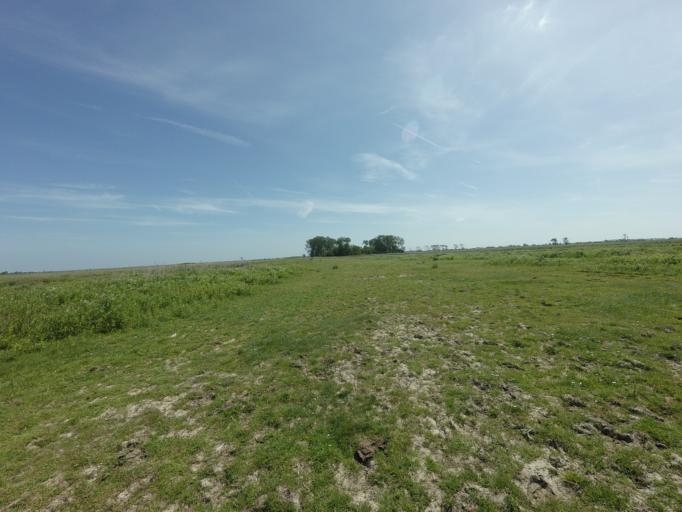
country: NL
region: South Holland
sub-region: Gemeente Spijkenisse
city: Spijkenisse
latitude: 51.7433
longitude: 4.3035
